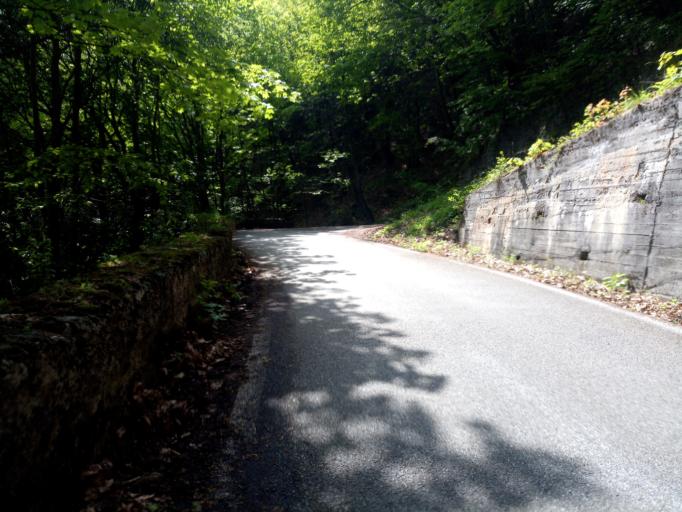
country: IT
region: Piedmont
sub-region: Provincia di Torino
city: Meana di Susa
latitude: 45.1119
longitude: 7.0621
